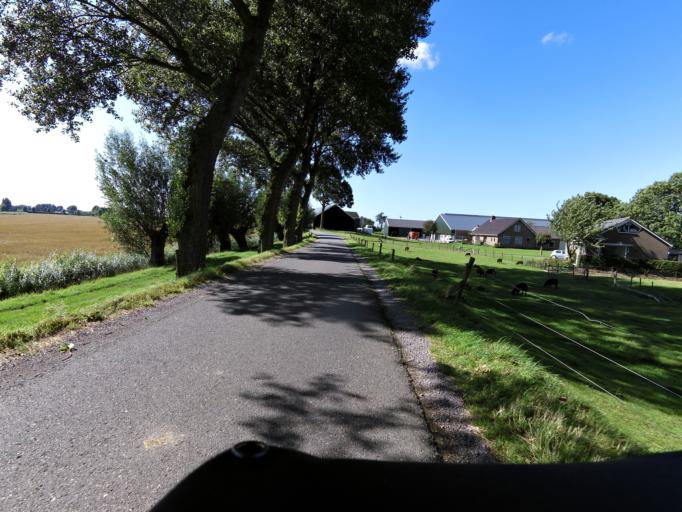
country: NL
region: South Holland
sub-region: Gemeente Spijkenisse
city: Spijkenisse
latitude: 51.8484
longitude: 4.2889
